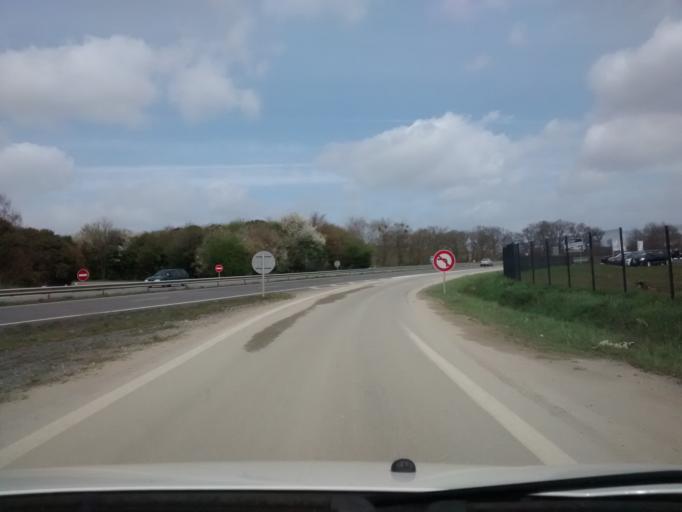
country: FR
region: Brittany
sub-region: Departement d'Ille-et-Vilaine
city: Bruz
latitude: 48.0452
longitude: -1.7539
